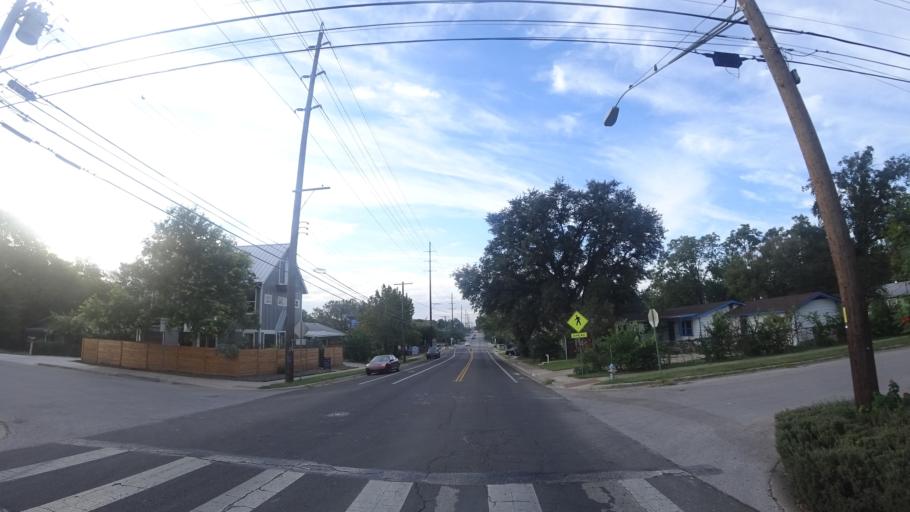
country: US
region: Texas
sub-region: Travis County
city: Austin
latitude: 30.2784
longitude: -97.7169
